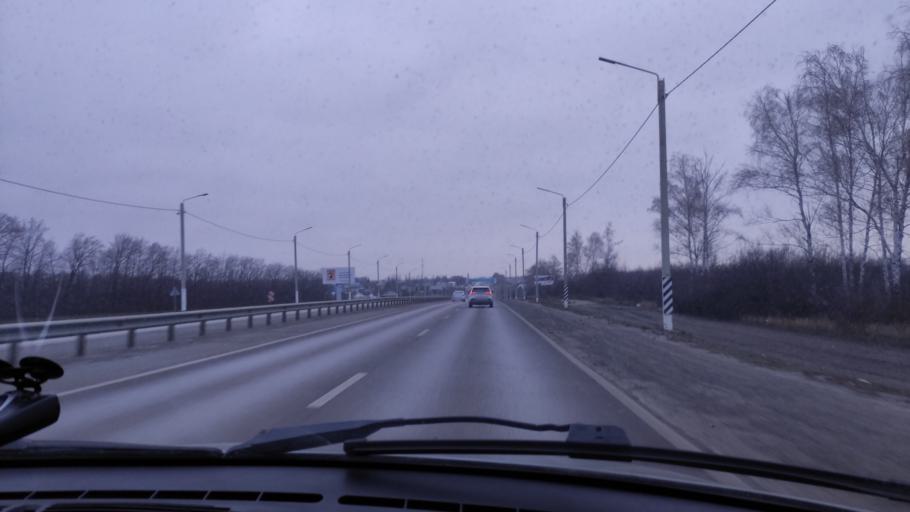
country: RU
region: Tambov
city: Komsomolets
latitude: 52.7273
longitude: 41.3360
